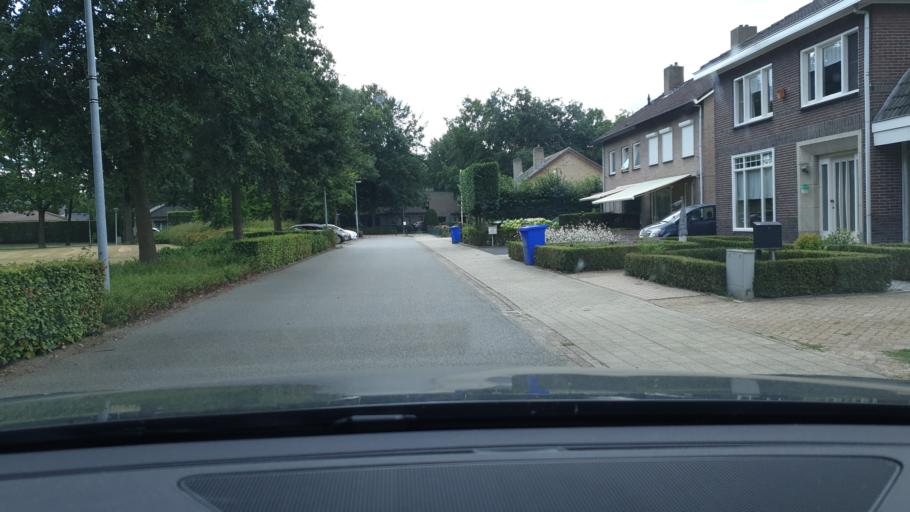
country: NL
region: North Brabant
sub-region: Gemeente Veldhoven
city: Oerle
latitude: 51.4240
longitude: 5.3758
